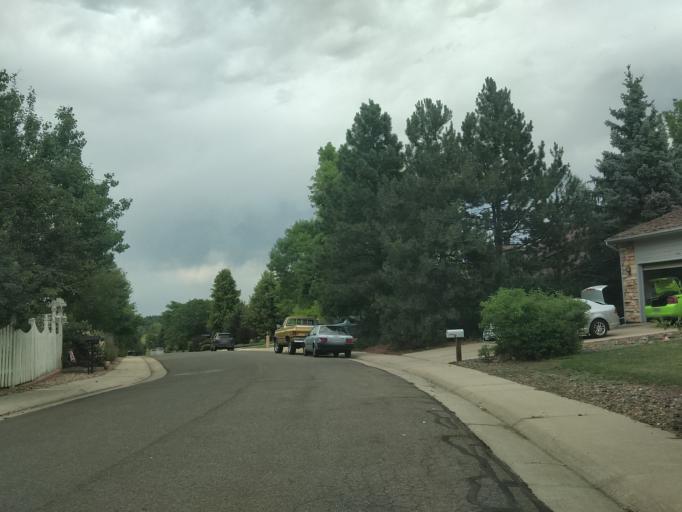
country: US
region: Colorado
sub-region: Jefferson County
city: Lakewood
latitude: 39.6970
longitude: -105.0905
